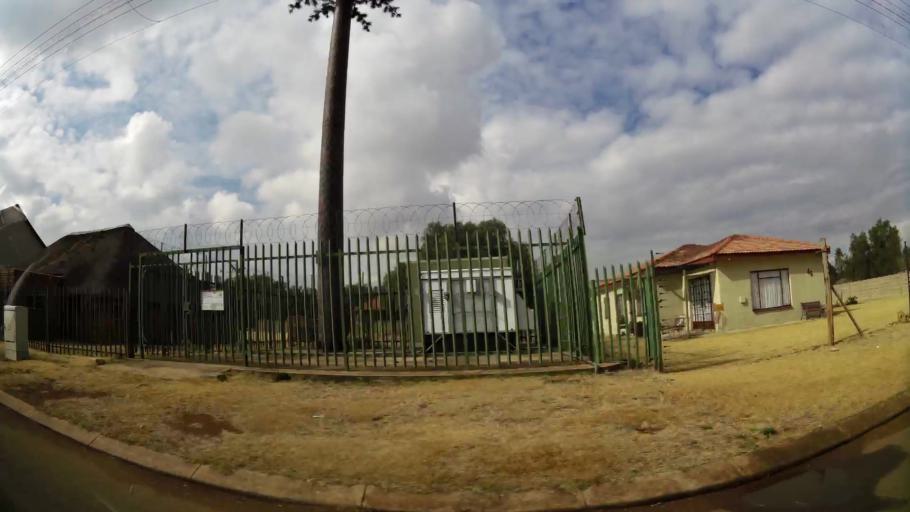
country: ZA
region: Gauteng
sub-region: Sedibeng District Municipality
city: Meyerton
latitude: -26.6005
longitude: 28.0392
